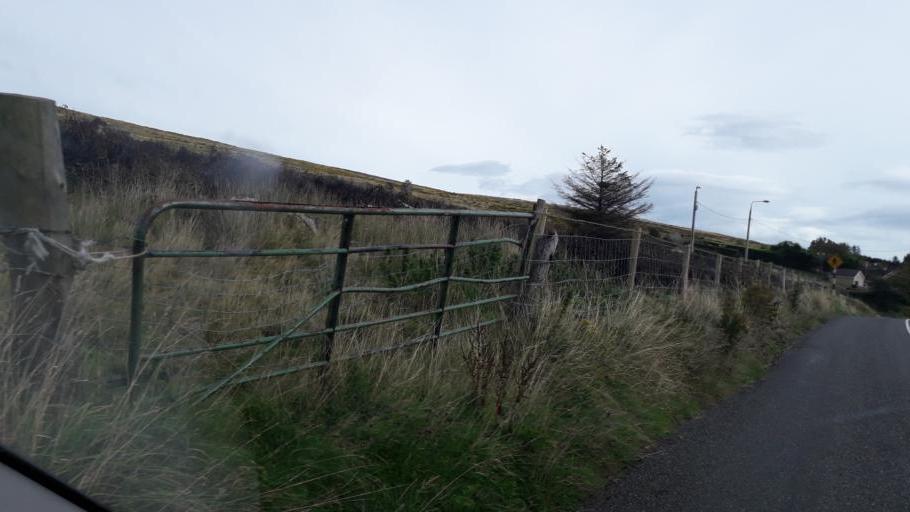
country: IE
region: Leinster
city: Ballinteer
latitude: 53.2256
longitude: -6.2461
